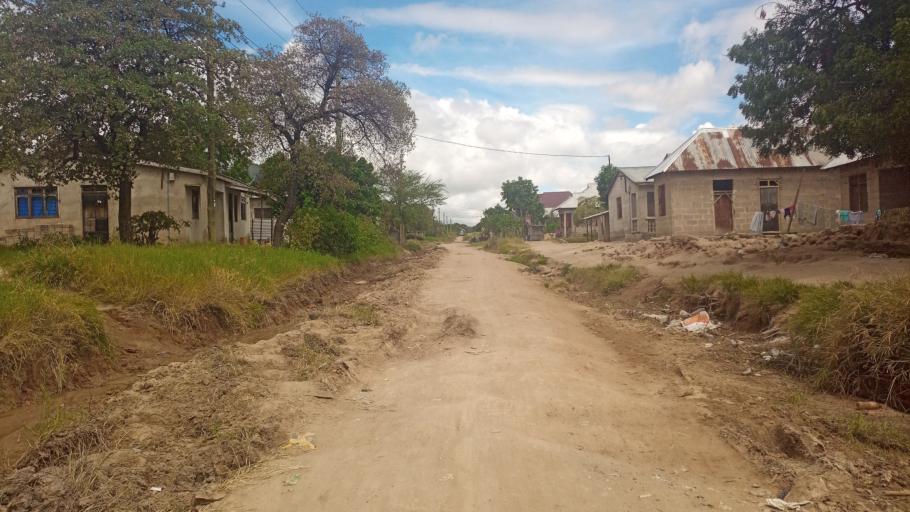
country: TZ
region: Dodoma
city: Dodoma
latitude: -6.1887
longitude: 35.7233
